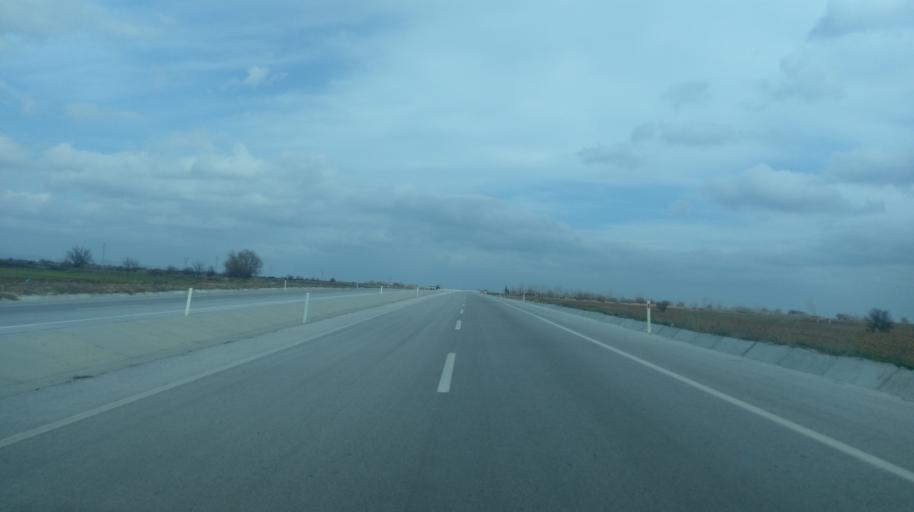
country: TR
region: Kirklareli
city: Inece
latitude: 41.6808
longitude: 27.1056
